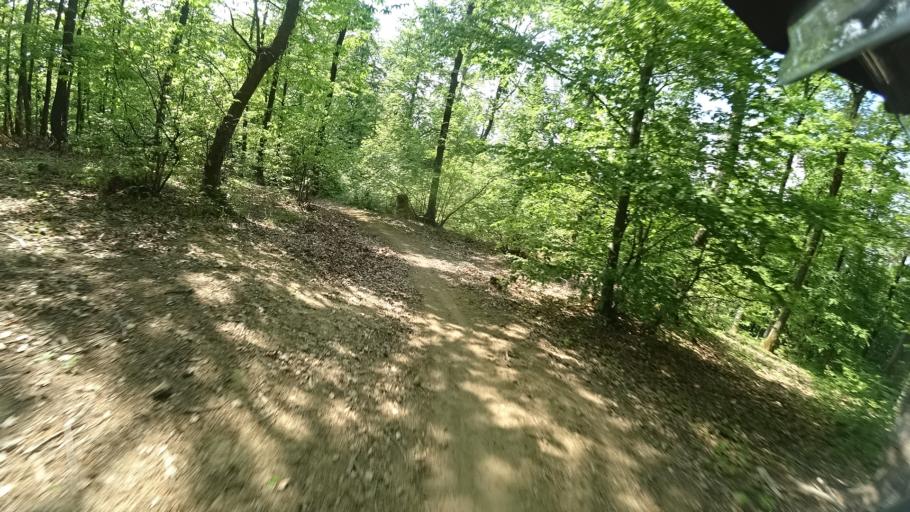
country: HR
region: Grad Zagreb
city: Kasina
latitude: 45.9446
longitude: 15.9633
